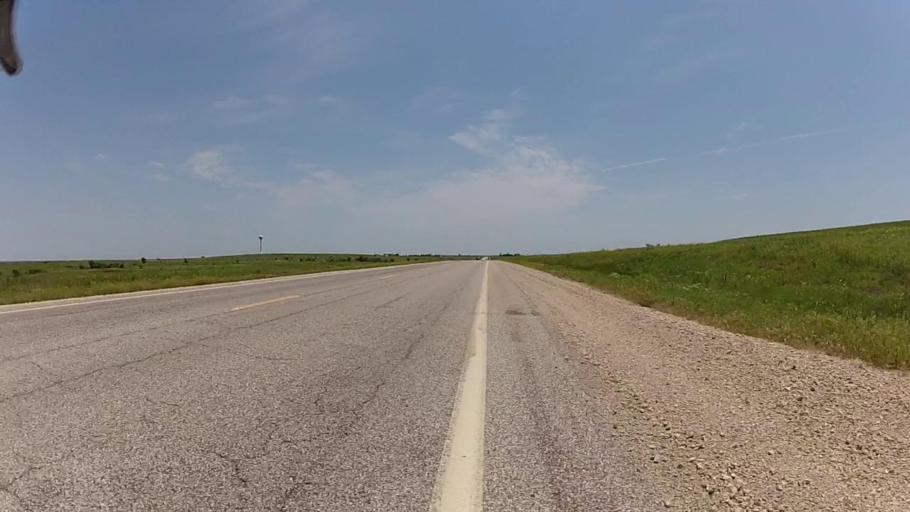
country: US
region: Kansas
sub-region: Chautauqua County
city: Sedan
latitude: 37.1098
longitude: -96.2538
